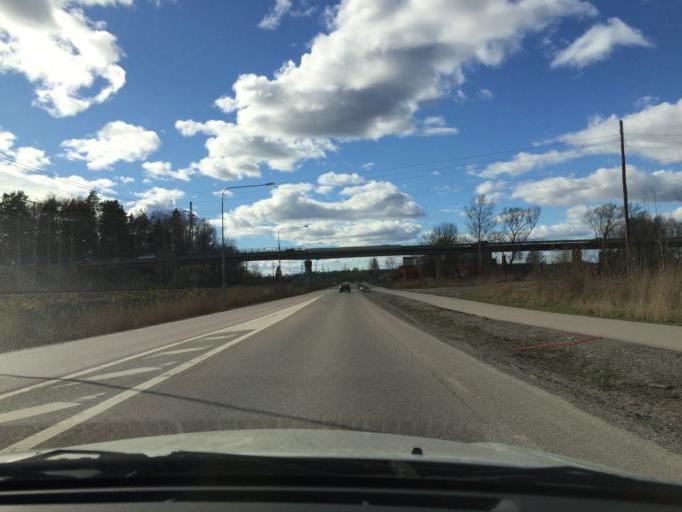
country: SE
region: Soedermanland
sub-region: Eskilstuna Kommun
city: Torshalla
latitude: 59.3834
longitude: 16.4650
